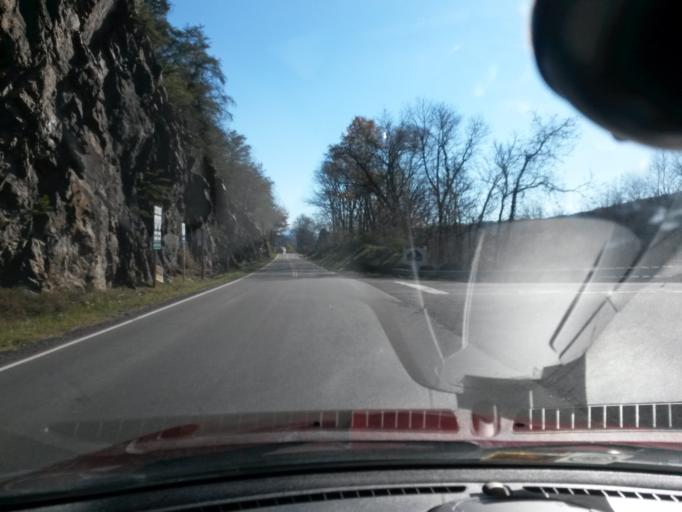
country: US
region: Virginia
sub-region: Botetourt County
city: Fincastle
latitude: 37.6426
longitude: -79.8053
